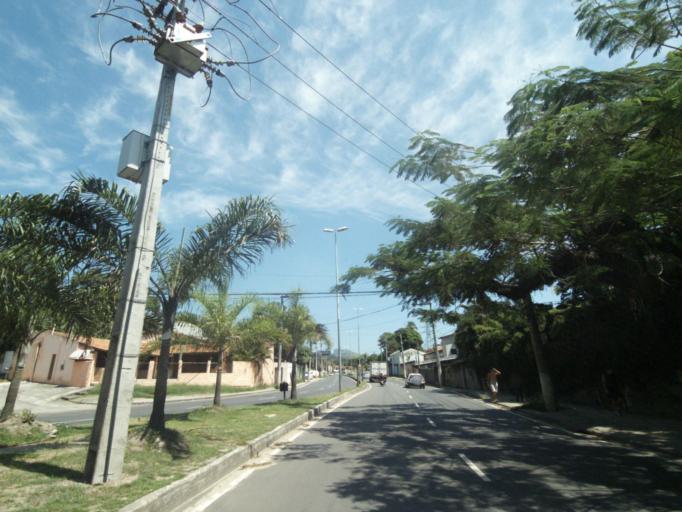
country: BR
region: Rio de Janeiro
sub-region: Sao Goncalo
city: Sao Goncalo
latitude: -22.8788
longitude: -43.0268
